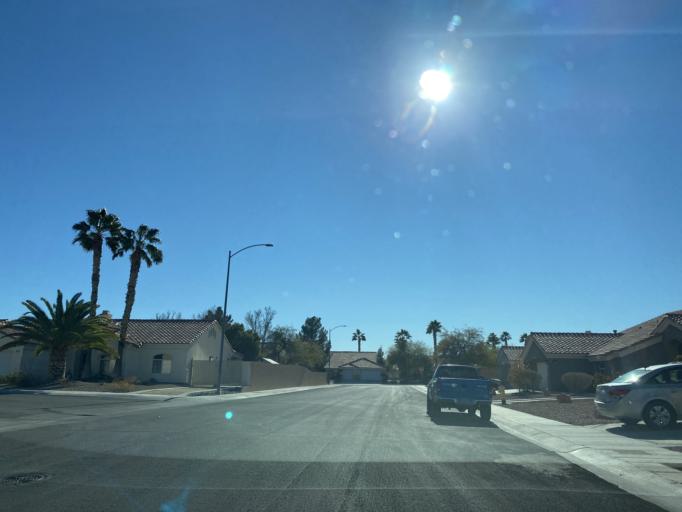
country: US
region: Nevada
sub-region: Clark County
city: Summerlin South
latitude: 36.2645
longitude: -115.2742
